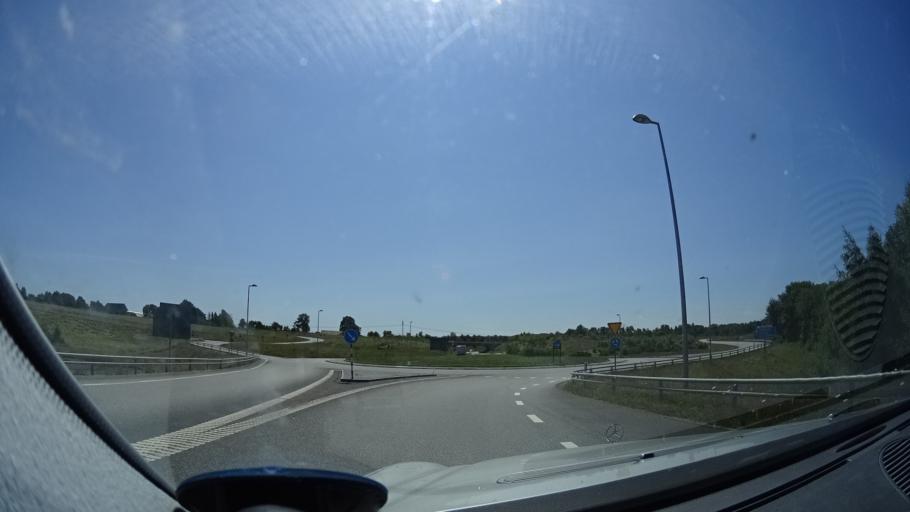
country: SE
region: Skane
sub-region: Hoors Kommun
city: Loberod
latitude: 55.8119
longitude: 13.4778
